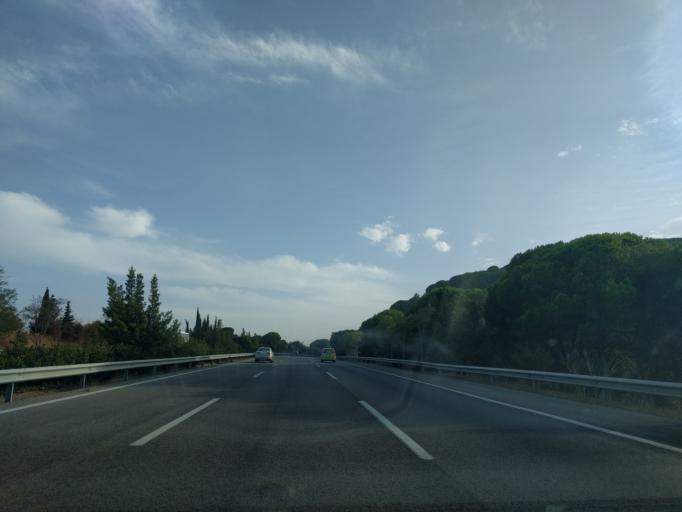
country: ES
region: Catalonia
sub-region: Provincia de Barcelona
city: Calella
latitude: 41.6167
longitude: 2.6420
